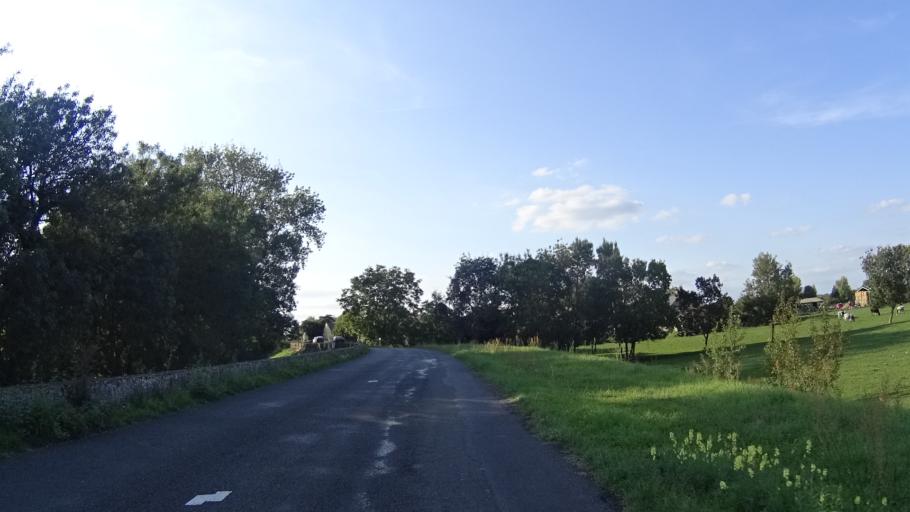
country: FR
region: Pays de la Loire
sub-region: Departement de Maine-et-Loire
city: Saint-Germain-des-Pres
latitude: 47.3902
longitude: -0.8299
